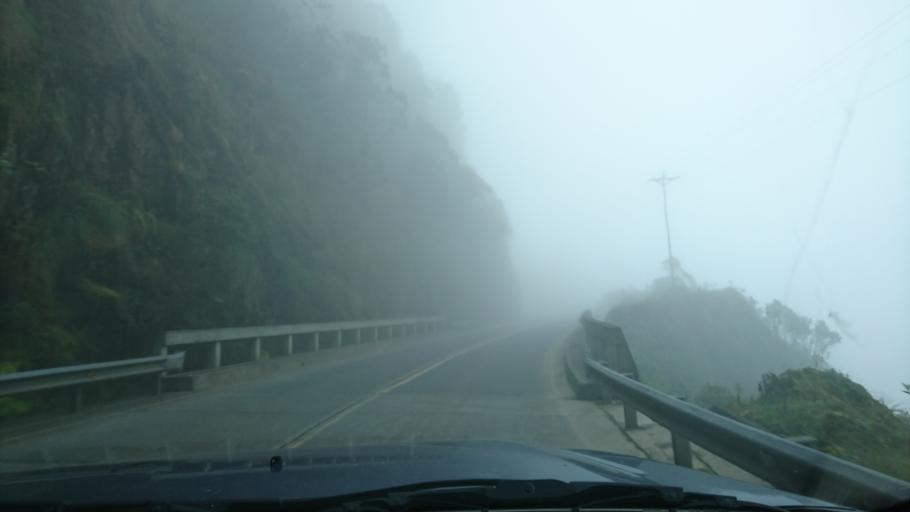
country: BO
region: La Paz
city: Coroico
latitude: -16.2798
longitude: -67.8263
